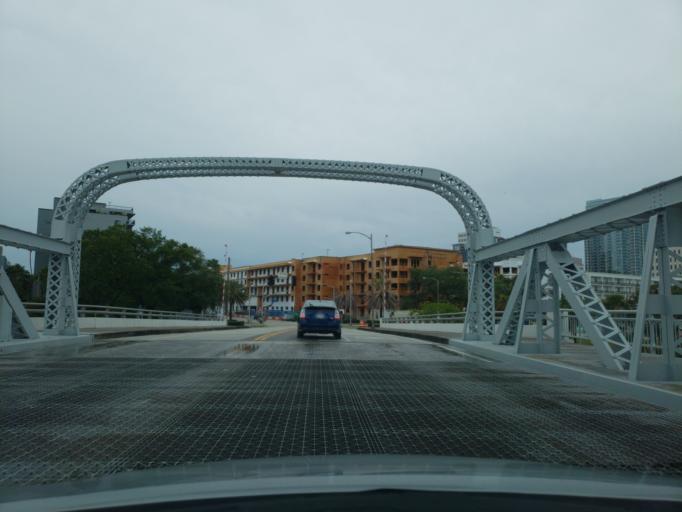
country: US
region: Florida
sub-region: Hillsborough County
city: Tampa
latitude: 27.9545
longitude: -82.4650
